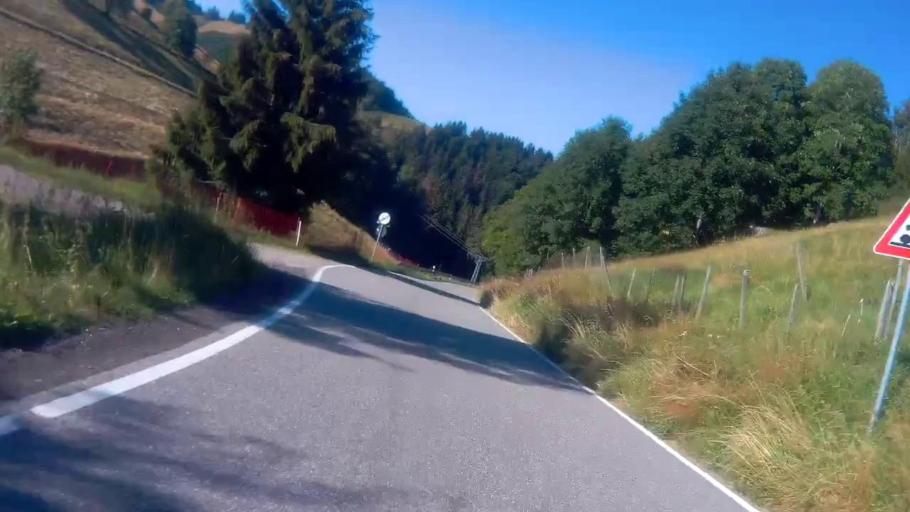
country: DE
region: Baden-Wuerttemberg
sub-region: Freiburg Region
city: Horben
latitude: 47.8921
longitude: 7.8748
